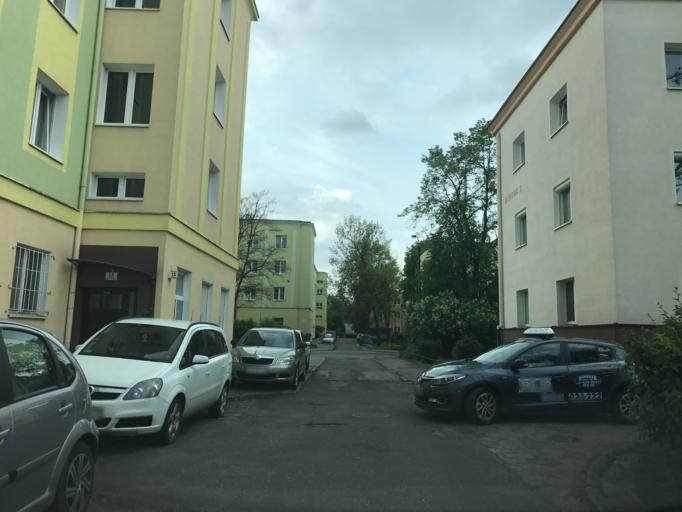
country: PL
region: Kujawsko-Pomorskie
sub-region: Bydgoszcz
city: Bydgoszcz
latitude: 53.1418
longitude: 18.0269
